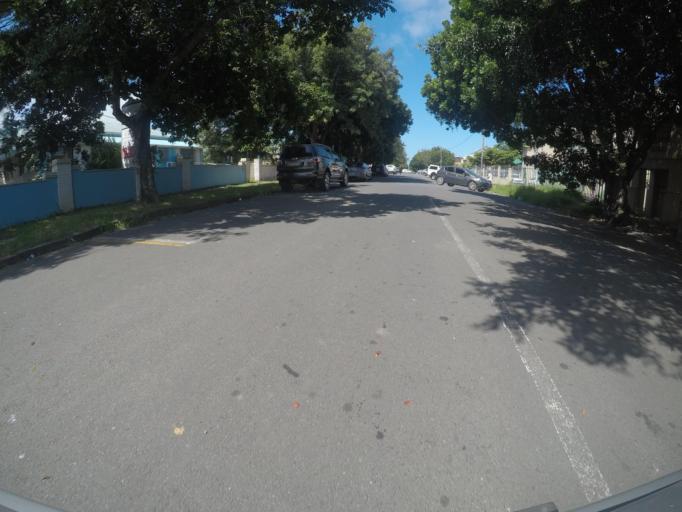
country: ZA
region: Eastern Cape
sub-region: Buffalo City Metropolitan Municipality
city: East London
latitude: -33.0030
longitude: 27.8960
